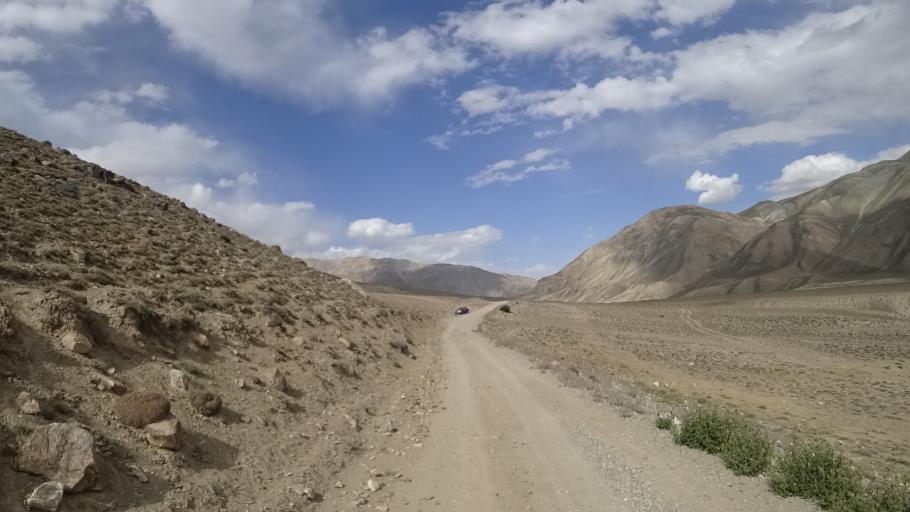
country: AF
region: Badakhshan
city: Khandud
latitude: 37.1923
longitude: 72.7639
